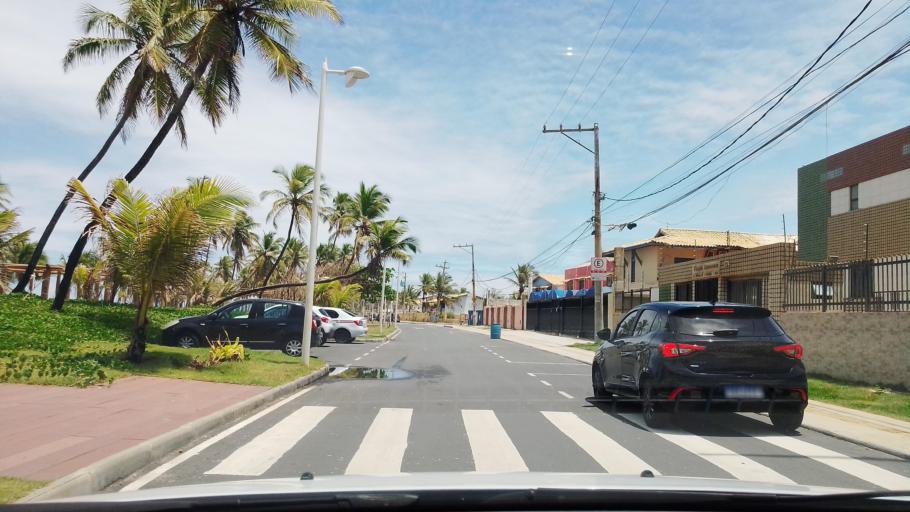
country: BR
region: Bahia
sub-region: Lauro De Freitas
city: Lauro de Freitas
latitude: -12.9397
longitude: -38.3309
